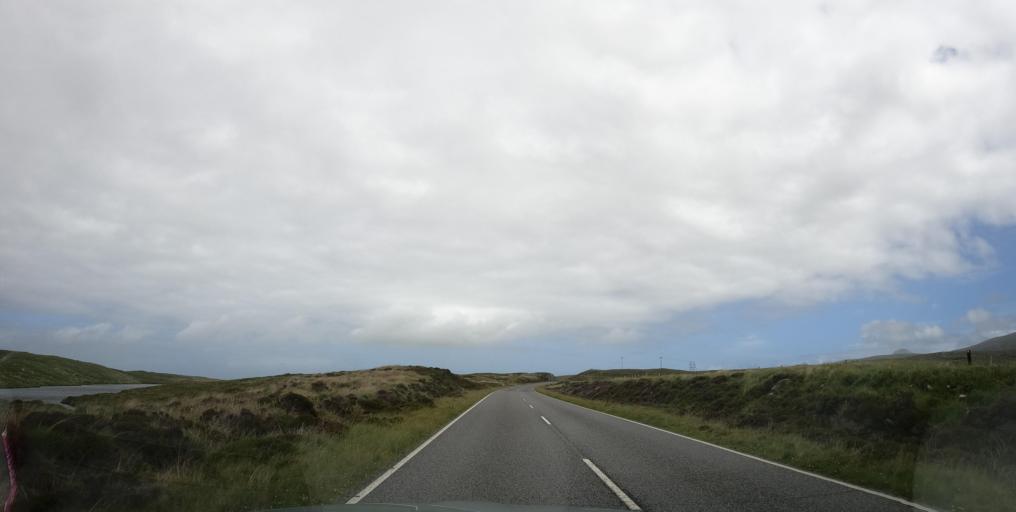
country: GB
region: Scotland
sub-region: Eilean Siar
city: Isle of South Uist
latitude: 57.2600
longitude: -7.3714
